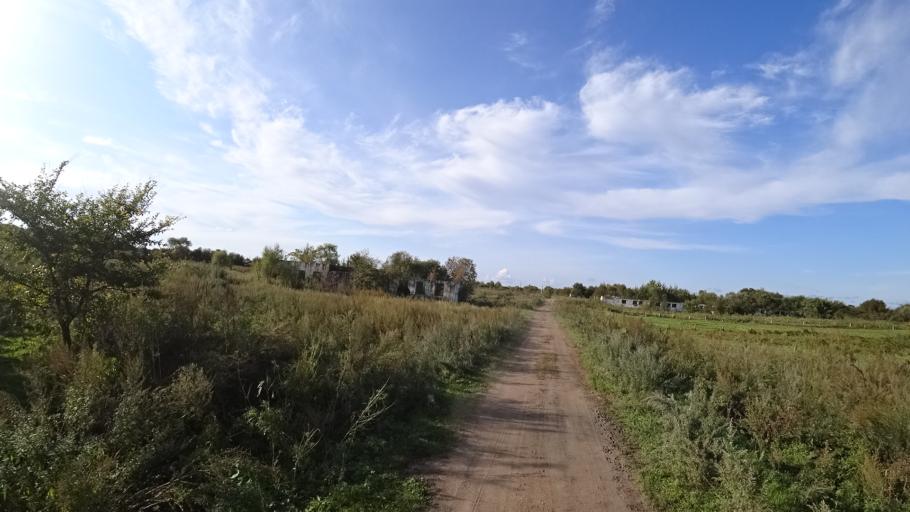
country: RU
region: Amur
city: Arkhara
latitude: 49.3478
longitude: 130.1068
